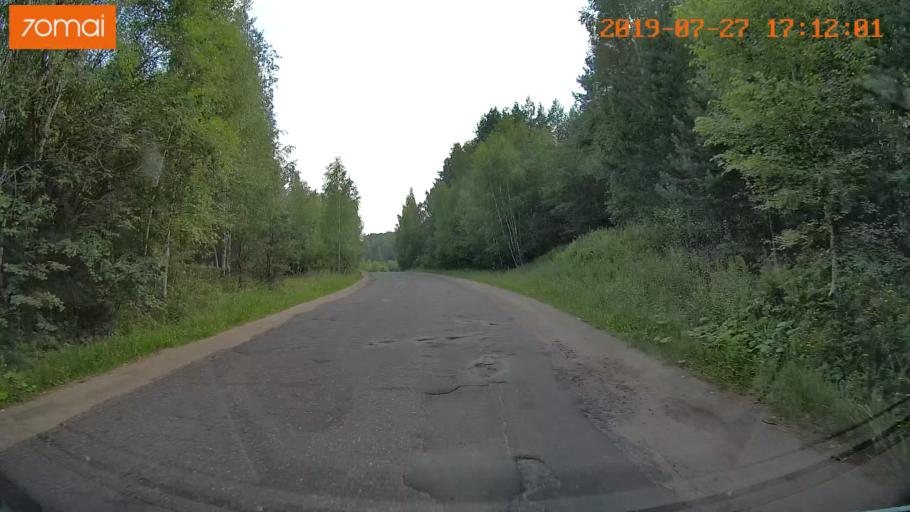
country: RU
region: Ivanovo
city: Novo-Talitsy
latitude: 57.0611
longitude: 40.8633
